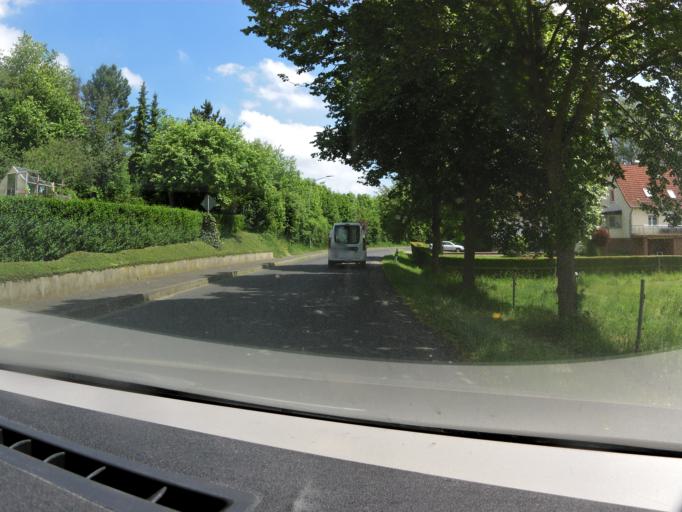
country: DE
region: Hesse
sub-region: Regierungsbezirk Kassel
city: Ronshausen
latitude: 50.9799
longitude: 9.8666
